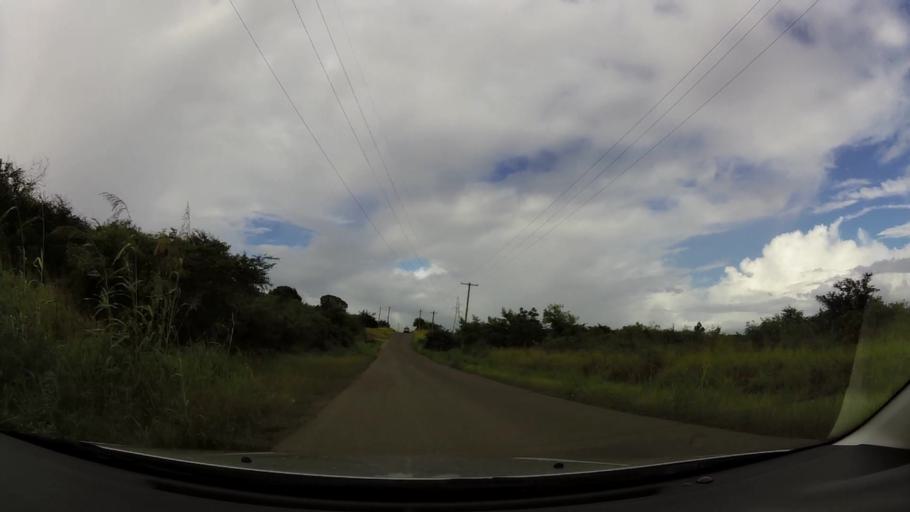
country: AG
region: Saint George
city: Piggotts
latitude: 17.1020
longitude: -61.8122
